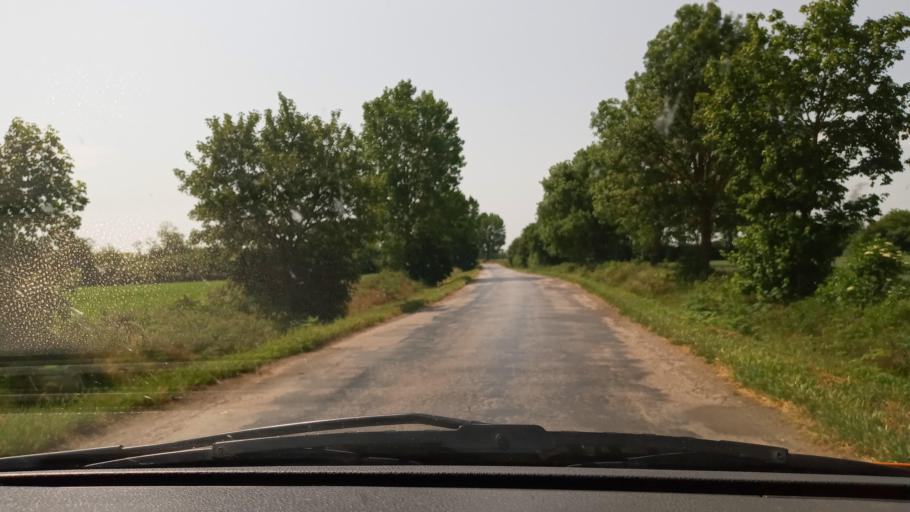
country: HU
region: Baranya
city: Szentlorinc
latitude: 46.0267
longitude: 18.0316
